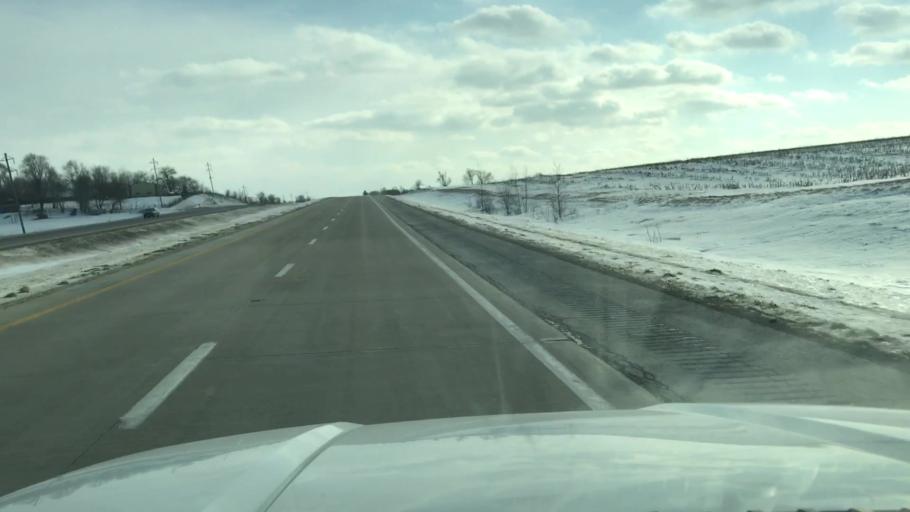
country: US
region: Missouri
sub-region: Nodaway County
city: Maryville
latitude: 40.2218
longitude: -94.8682
